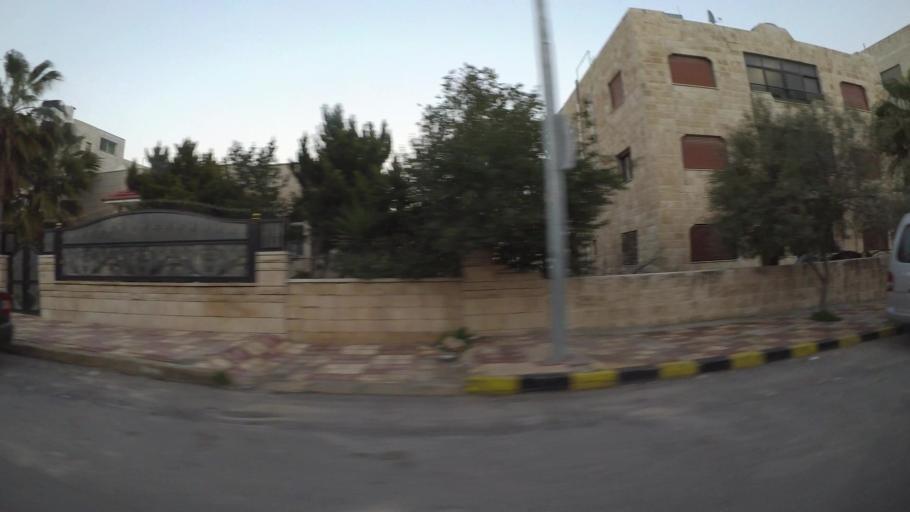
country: JO
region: Amman
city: Amman
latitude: 31.9906
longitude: 35.9716
